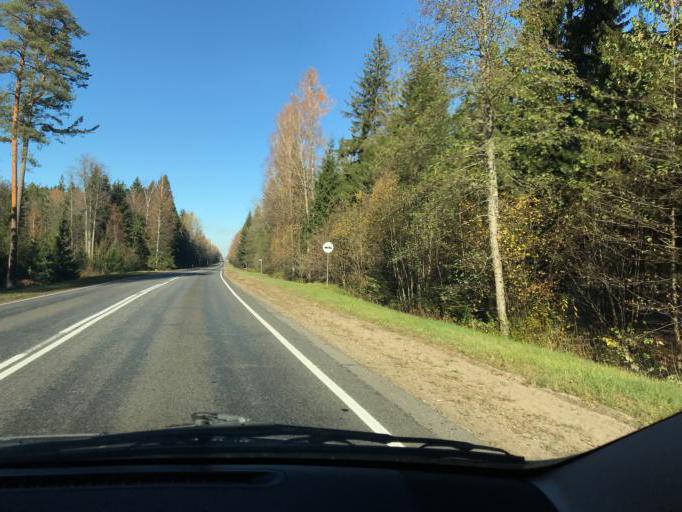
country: BY
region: Vitebsk
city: Polatsk
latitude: 55.4191
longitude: 28.7921
